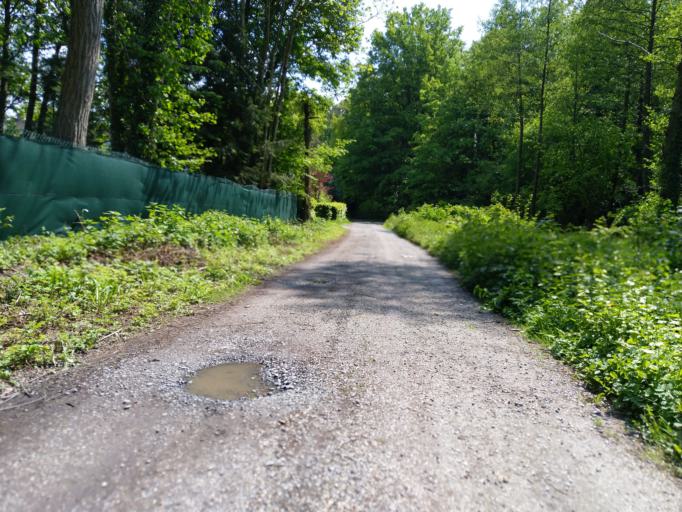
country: BE
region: Wallonia
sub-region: Province du Hainaut
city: Mons
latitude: 50.4992
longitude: 3.9912
